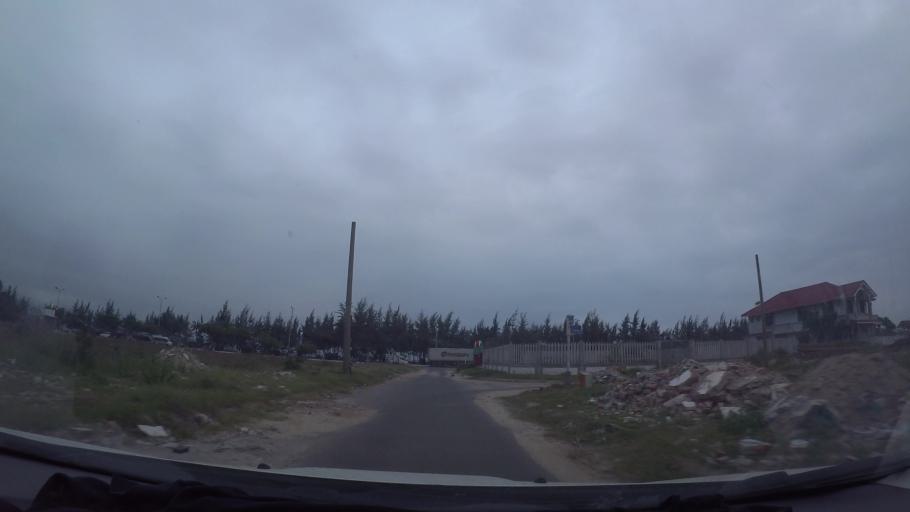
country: VN
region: Da Nang
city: Lien Chieu
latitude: 16.0891
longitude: 108.1522
